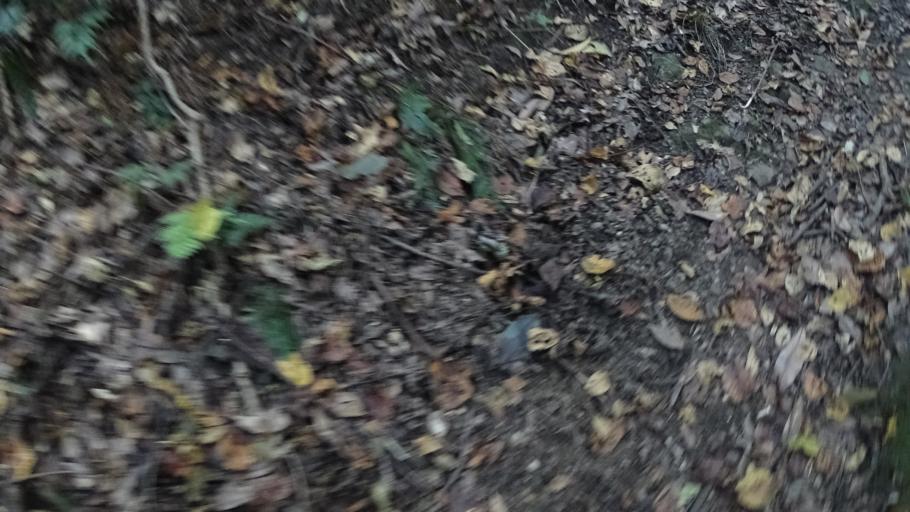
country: JP
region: Kanagawa
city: Zushi
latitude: 35.2846
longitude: 139.5925
